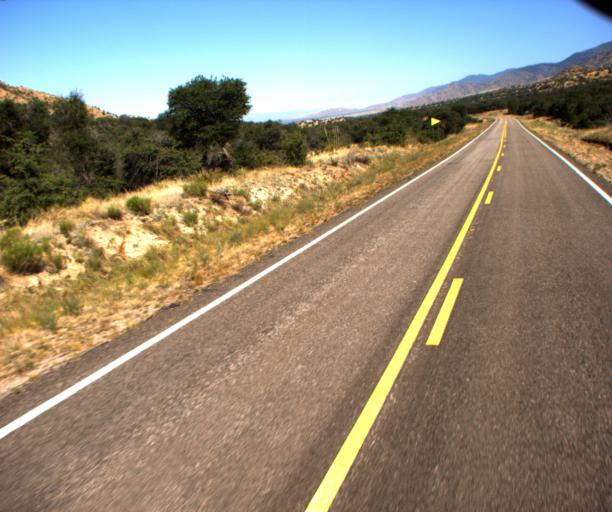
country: US
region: Arizona
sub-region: Graham County
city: Swift Trail Junction
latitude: 32.5939
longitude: -109.8567
